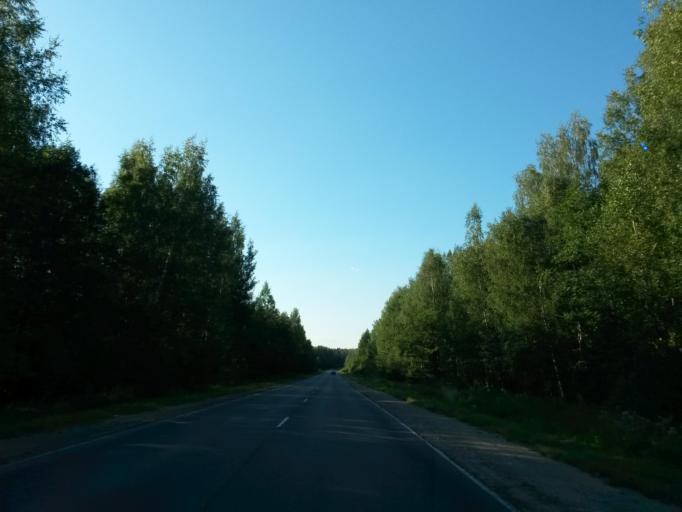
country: RU
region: Ivanovo
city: Pistsovo
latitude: 57.0982
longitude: 40.6574
